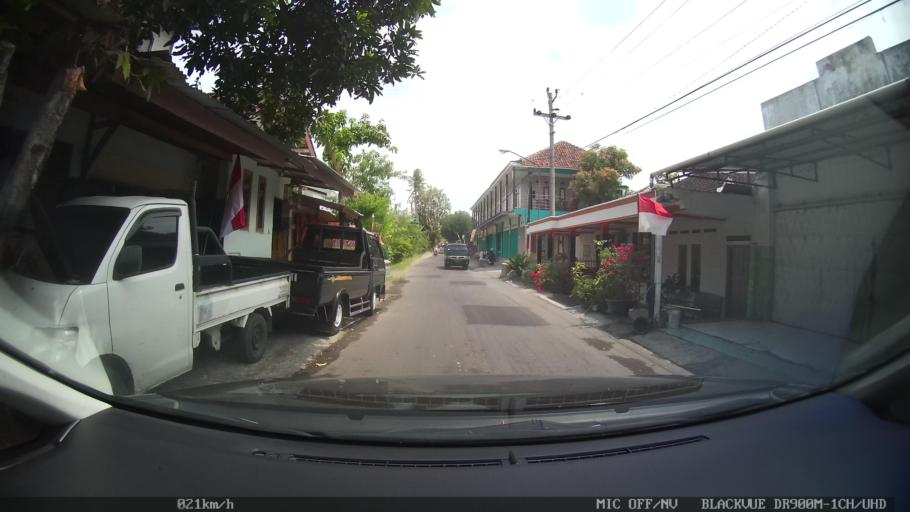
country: ID
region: Central Java
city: Candi Prambanan
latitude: -7.7815
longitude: 110.4853
